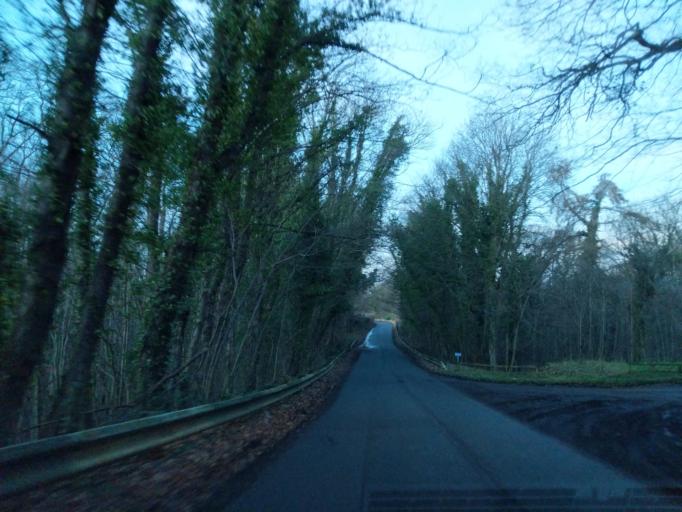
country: GB
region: Scotland
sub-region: Midlothian
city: Bonnyrigg
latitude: 55.8433
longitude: -3.0909
